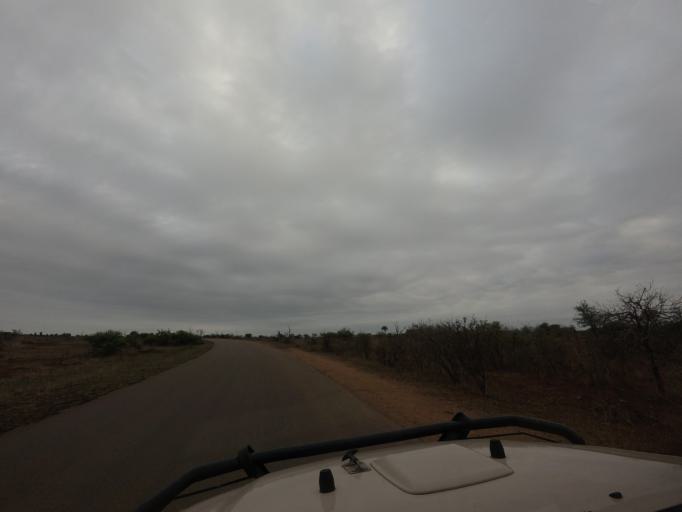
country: ZA
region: Mpumalanga
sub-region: Ehlanzeni District
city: Komatipoort
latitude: -25.3544
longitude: 31.8894
